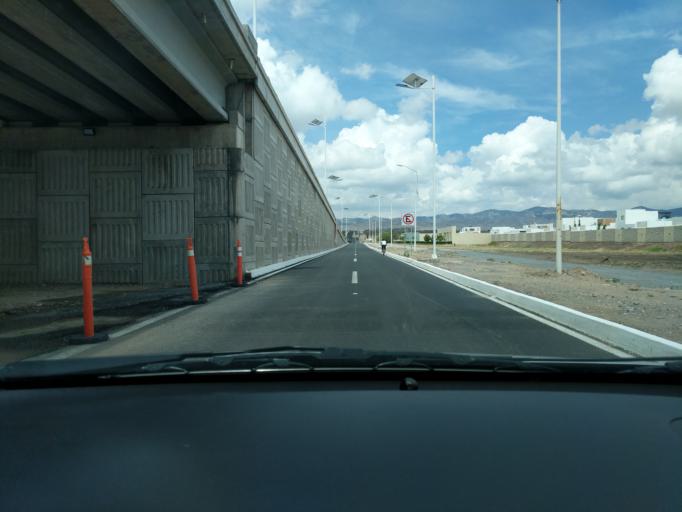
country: MX
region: San Luis Potosi
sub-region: Mexquitic de Carmona
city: Guadalupe Victoria
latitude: 22.1672
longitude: -101.0484
